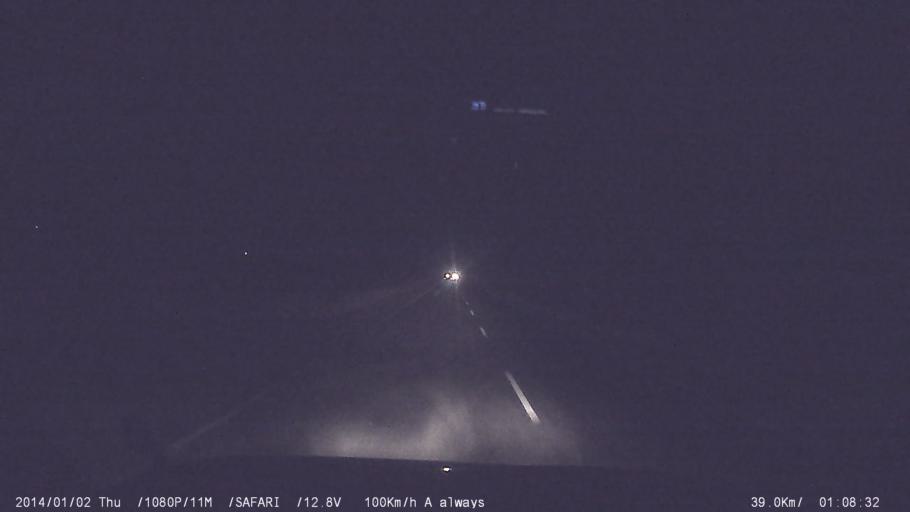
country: IN
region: Tamil Nadu
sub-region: Coimbatore
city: Chettipalaiyam
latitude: 10.9344
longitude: 77.0022
